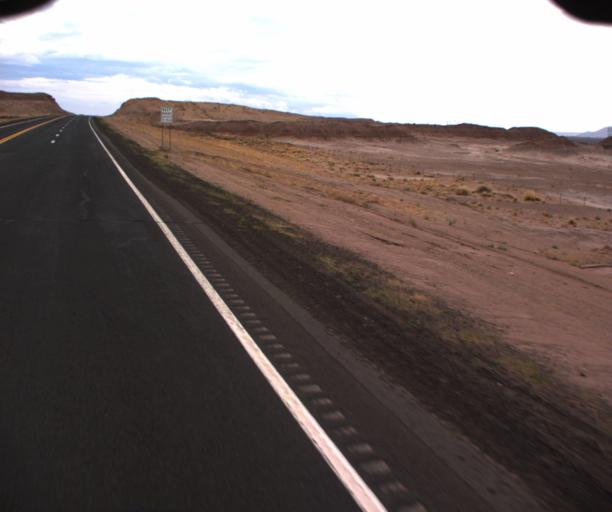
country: US
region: Arizona
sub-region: Coconino County
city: Tuba City
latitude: 35.9990
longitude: -111.3932
